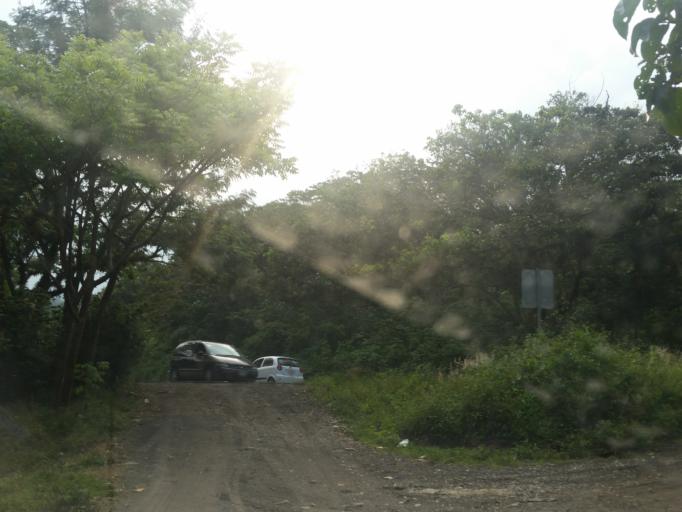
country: MX
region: Veracruz
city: Coatepec
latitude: 19.4292
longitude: -96.9610
